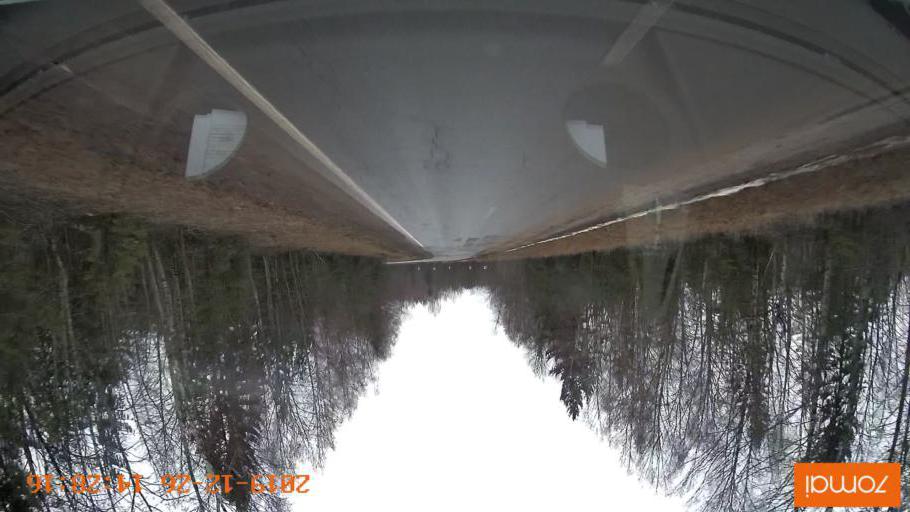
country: RU
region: Jaroslavl
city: Poshekhon'ye
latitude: 58.4771
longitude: 39.0550
